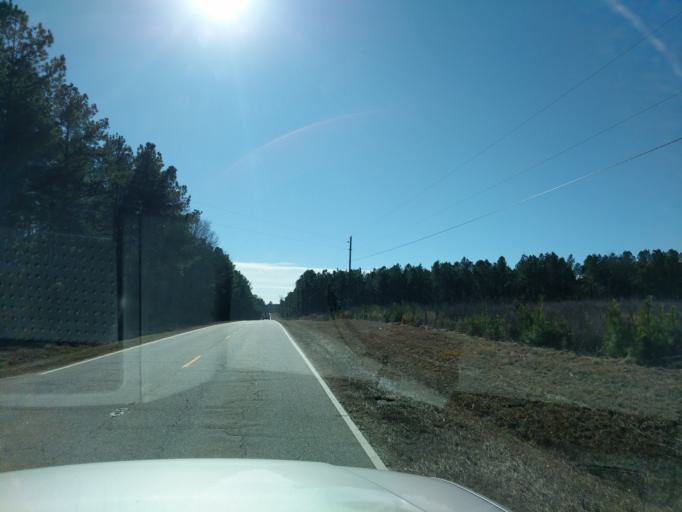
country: US
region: South Carolina
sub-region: Saluda County
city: Saluda
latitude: 34.1029
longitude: -81.8298
